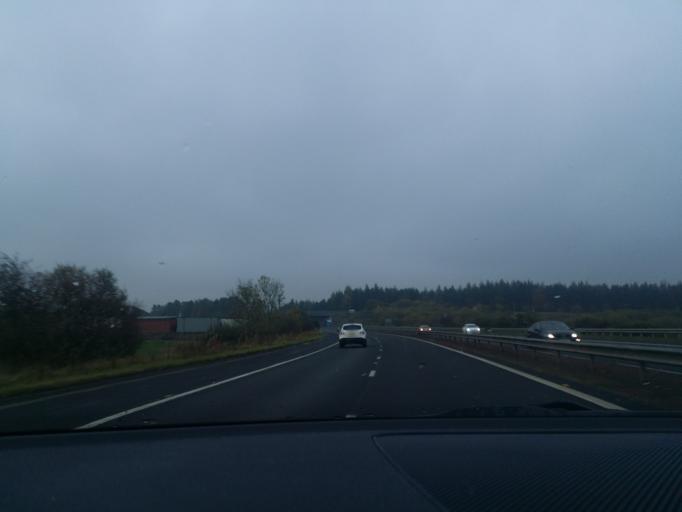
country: GB
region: Scotland
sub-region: Falkirk
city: Larbert
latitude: 56.0453
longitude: -3.8251
